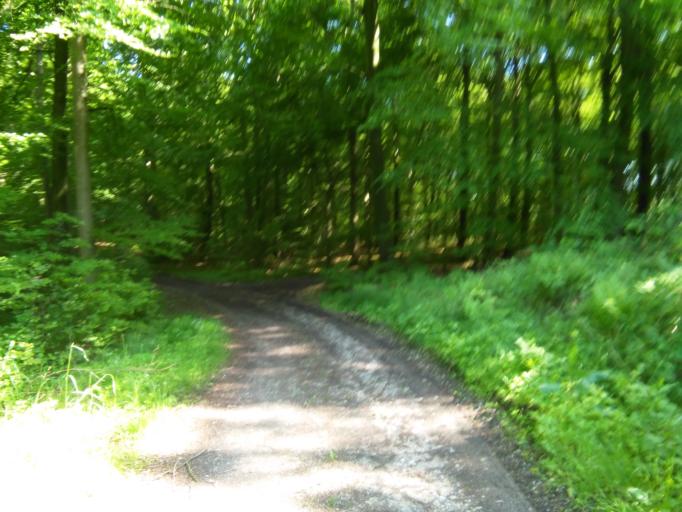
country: DK
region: Central Jutland
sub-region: Arhus Kommune
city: Malling
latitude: 56.0233
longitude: 10.1629
